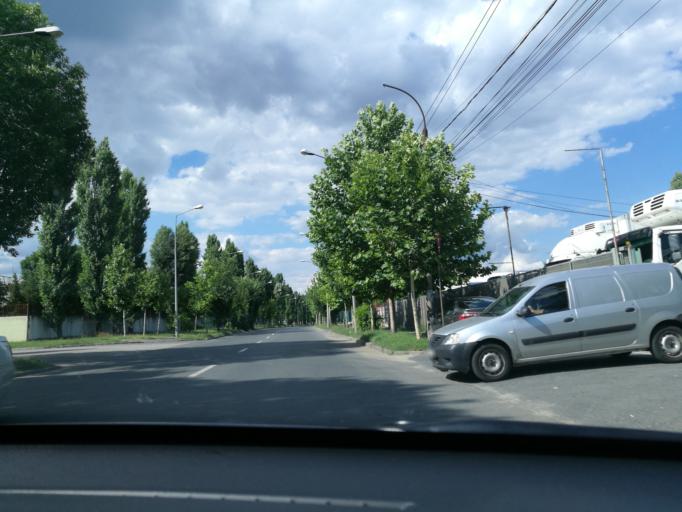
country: RO
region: Ilfov
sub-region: Comuna Glina
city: Catelu
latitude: 44.4220
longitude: 26.2193
